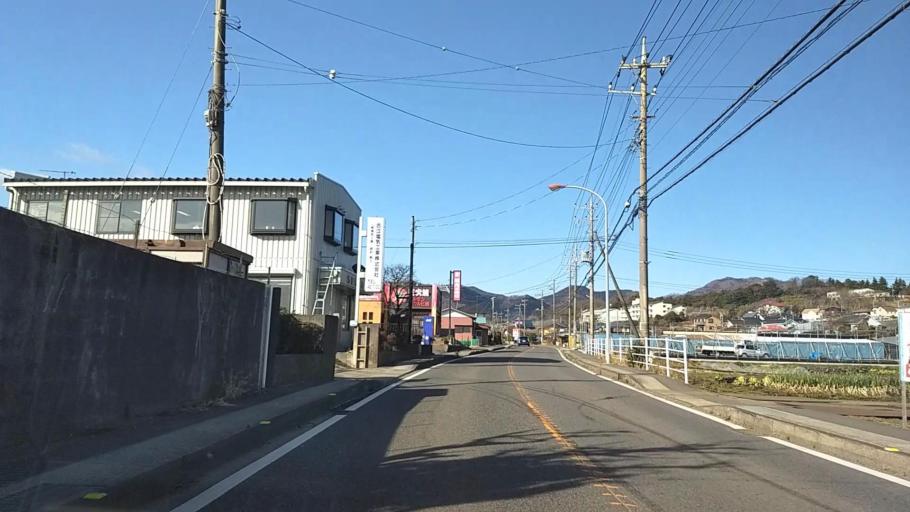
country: JP
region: Kanagawa
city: Atsugi
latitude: 35.4699
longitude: 139.3257
